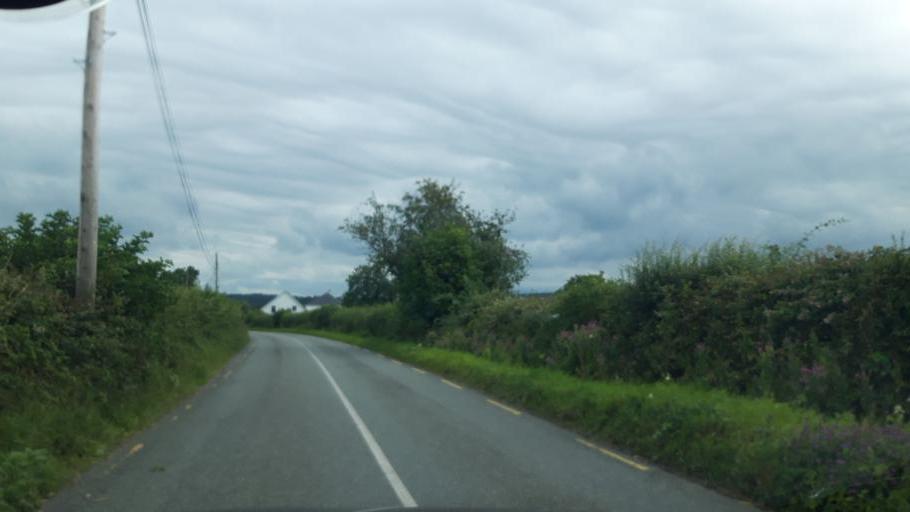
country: IE
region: Leinster
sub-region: Kilkenny
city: Ballyragget
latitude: 52.7412
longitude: -7.3985
